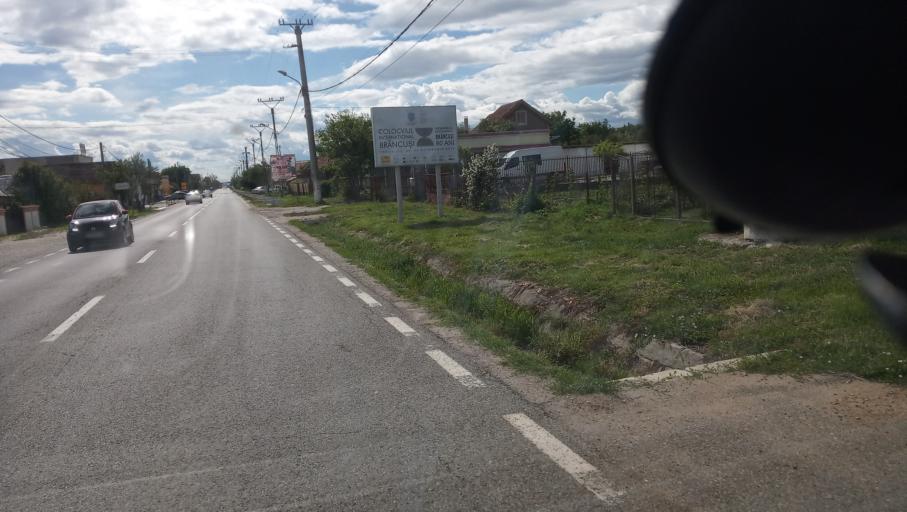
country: RO
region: Gorj
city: Targu Jiu
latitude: 45.0414
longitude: 23.3316
